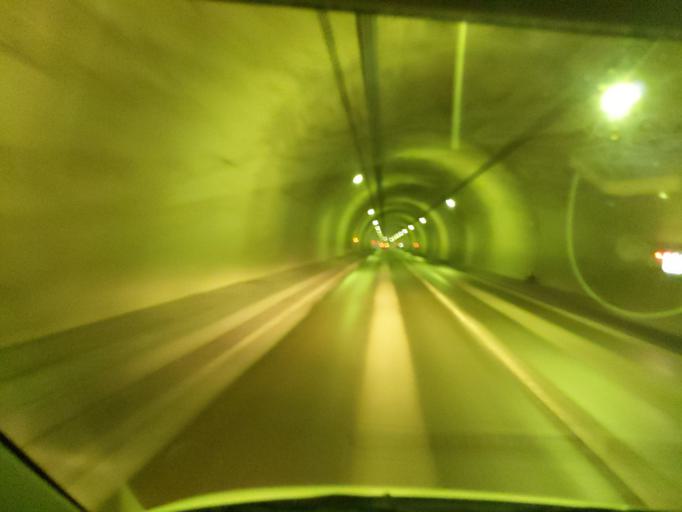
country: JP
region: Iwate
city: Tono
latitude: 39.1730
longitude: 141.3674
